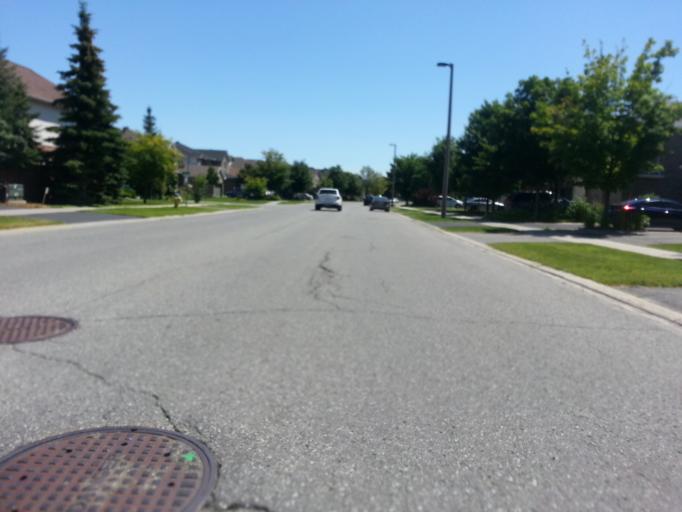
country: CA
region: Ontario
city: Bells Corners
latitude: 45.3198
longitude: -75.9268
